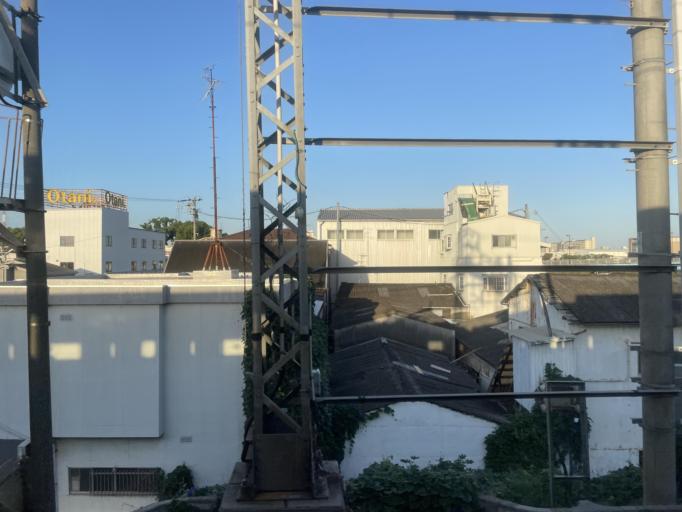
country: JP
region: Osaka
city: Matsubara
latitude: 34.5965
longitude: 135.5326
